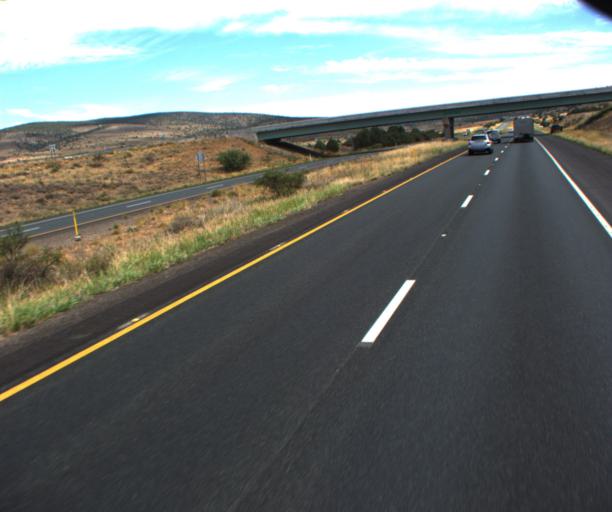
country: US
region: Arizona
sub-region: Yavapai County
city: Camp Verde
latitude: 34.5133
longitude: -111.9928
